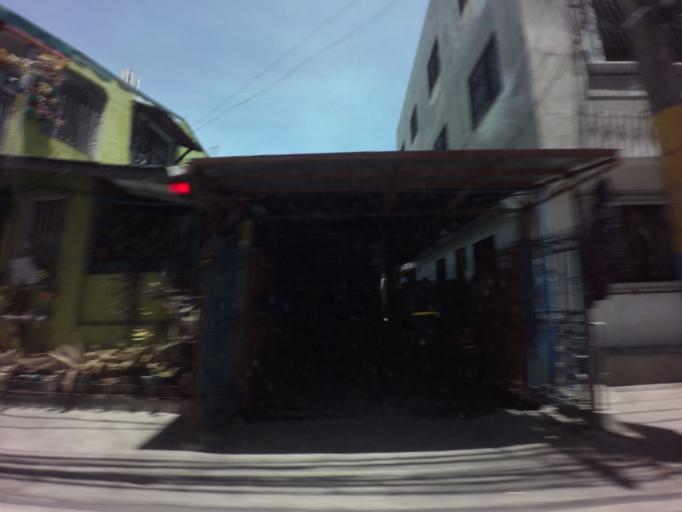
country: PH
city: Sambayanihan People's Village
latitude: 14.4507
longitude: 121.0515
